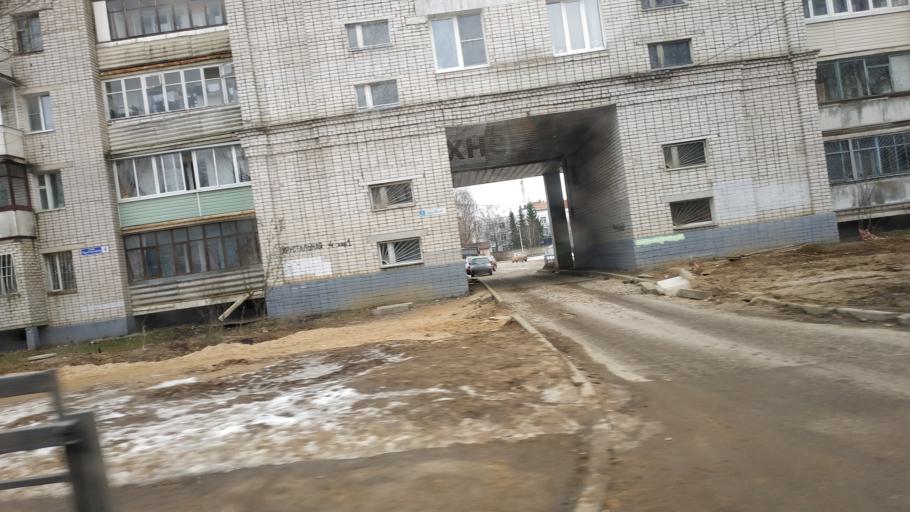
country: RU
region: Tverskaya
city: Tver
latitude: 56.8838
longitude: 35.9013
